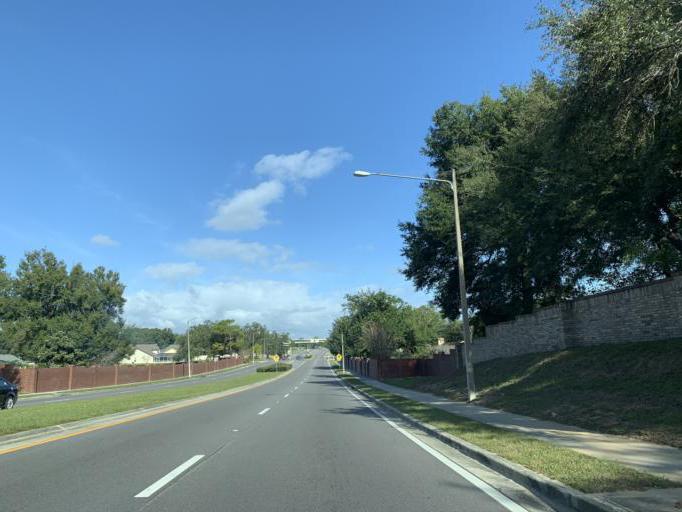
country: US
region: Florida
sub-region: Orange County
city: Clarcona
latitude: 28.6290
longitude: -81.4764
